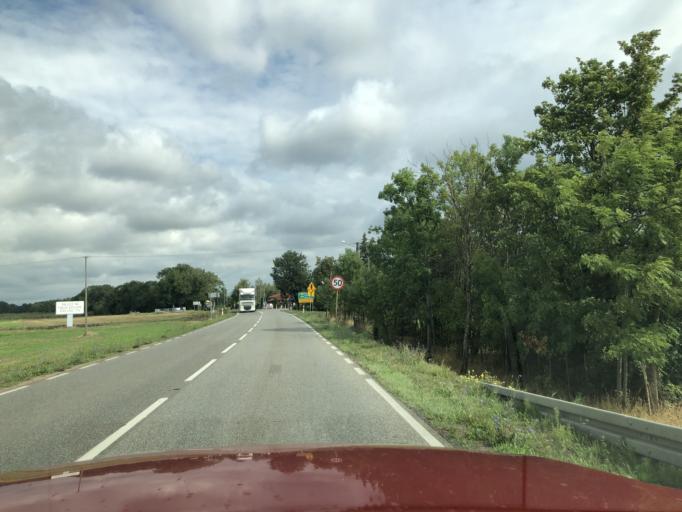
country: PL
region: Greater Poland Voivodeship
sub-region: Powiat szamotulski
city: Pniewy
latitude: 52.5356
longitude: 16.2799
